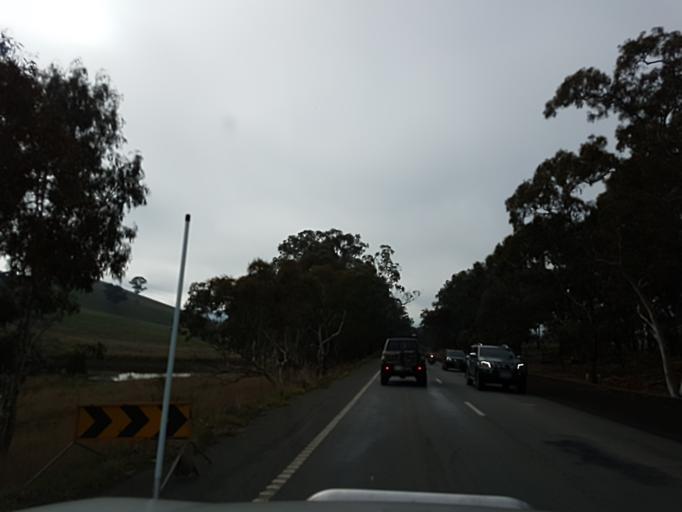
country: AU
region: Victoria
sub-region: Murrindindi
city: Alexandra
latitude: -37.1801
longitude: 145.4944
